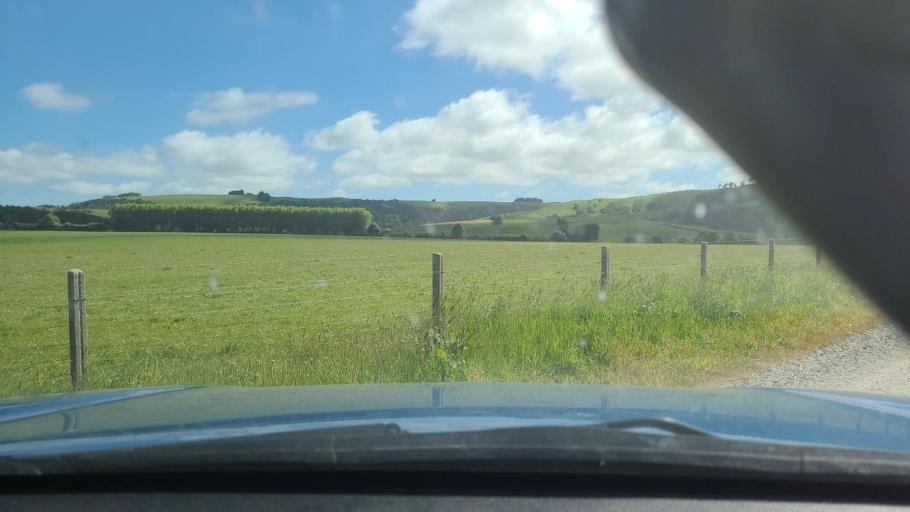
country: NZ
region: Southland
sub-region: Gore District
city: Gore
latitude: -46.3298
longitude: 168.9457
